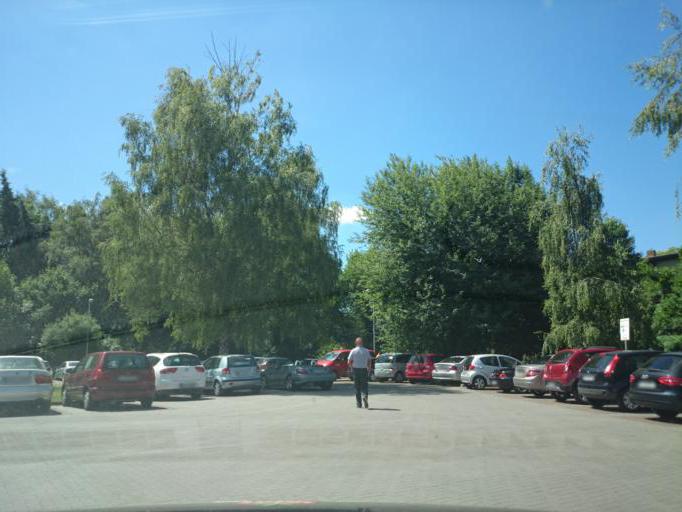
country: DE
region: Berlin
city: Lichtenrade
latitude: 52.3863
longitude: 13.4006
